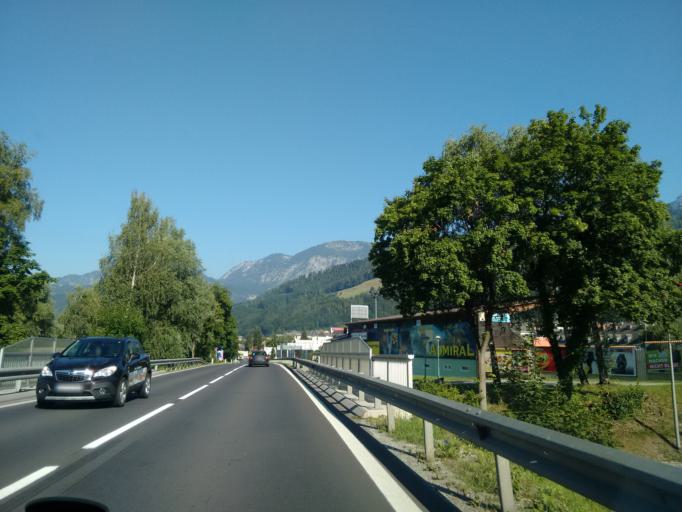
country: AT
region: Styria
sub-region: Politischer Bezirk Liezen
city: Liezen
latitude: 47.5655
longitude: 14.2379
